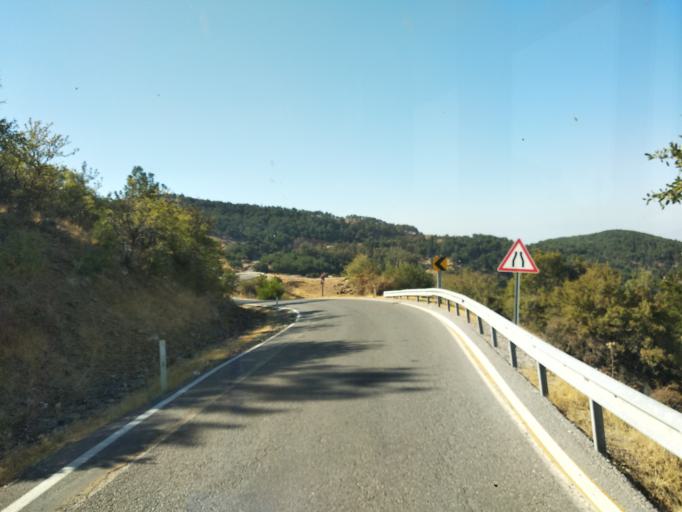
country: TR
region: Izmir
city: Gaziemir
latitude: 38.3244
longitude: 27.0066
